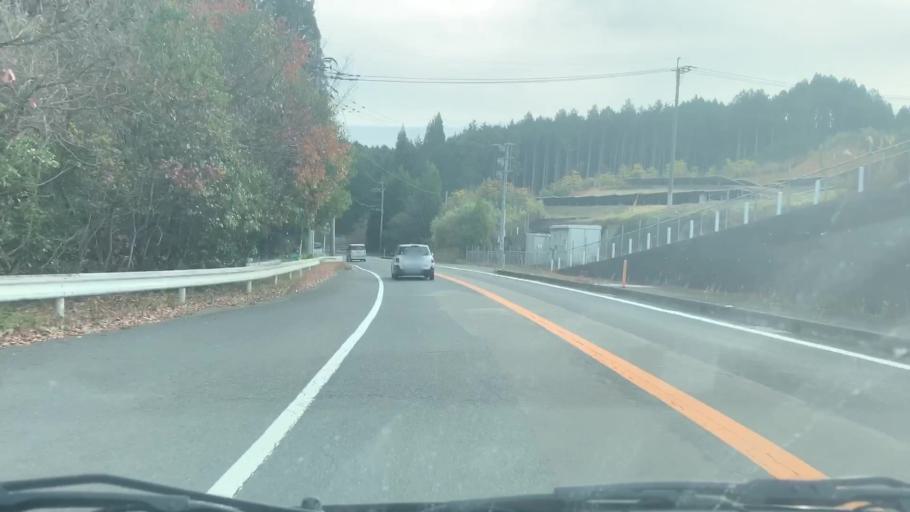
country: JP
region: Saga Prefecture
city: Karatsu
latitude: 33.3416
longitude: 129.9844
